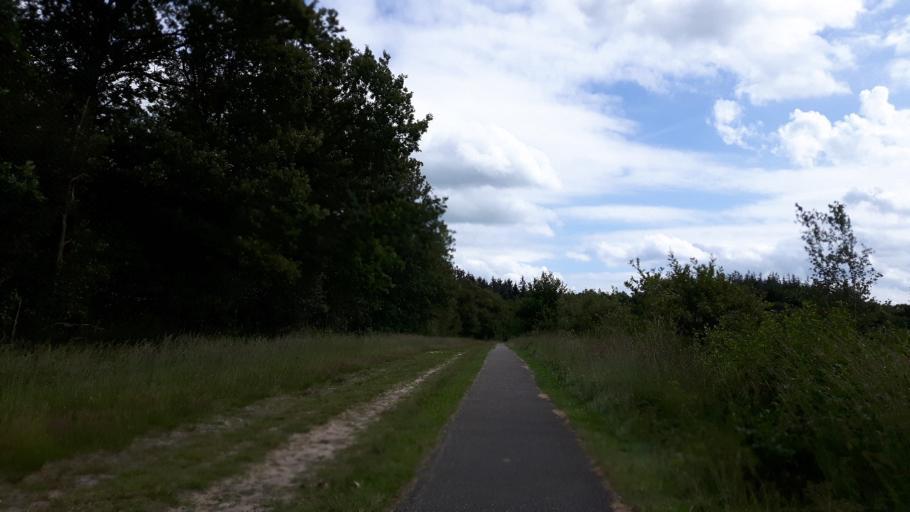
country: NL
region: Friesland
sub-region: Gemeente Smallingerland
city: Drachtstercompagnie
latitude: 53.0588
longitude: 6.2426
